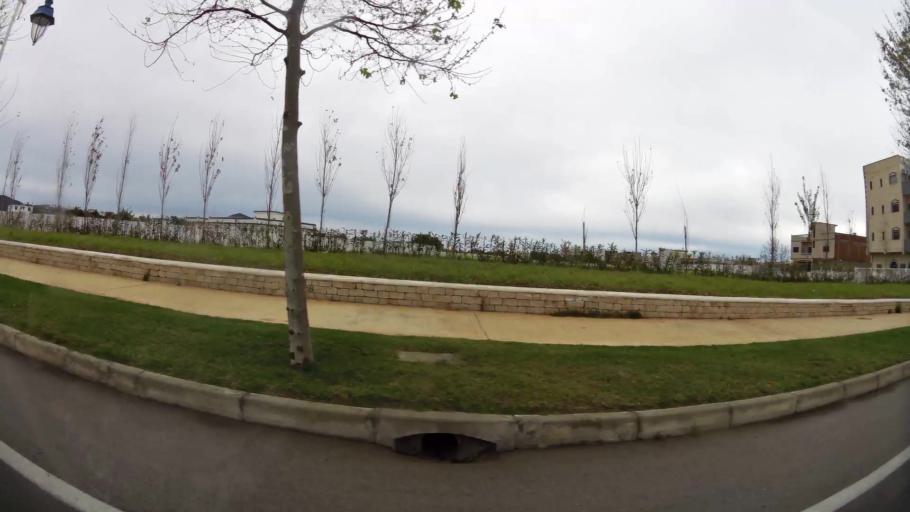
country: MA
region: Tanger-Tetouan
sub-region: Tetouan
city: Martil
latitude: 35.6391
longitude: -5.2909
